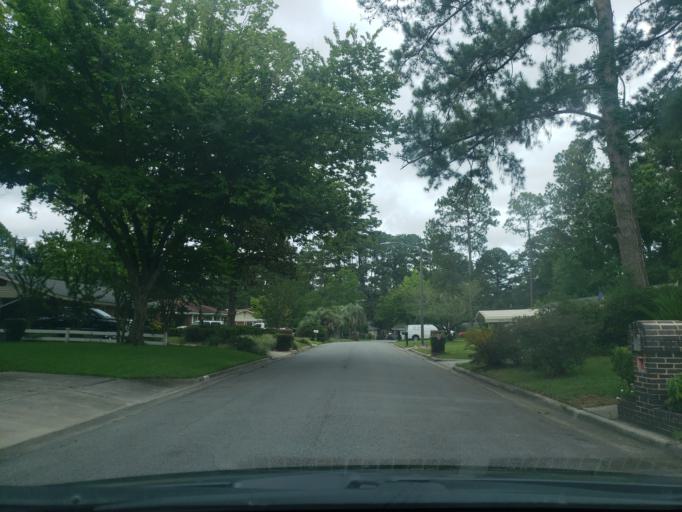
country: US
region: Georgia
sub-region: Chatham County
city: Montgomery
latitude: 31.9918
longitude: -81.1157
